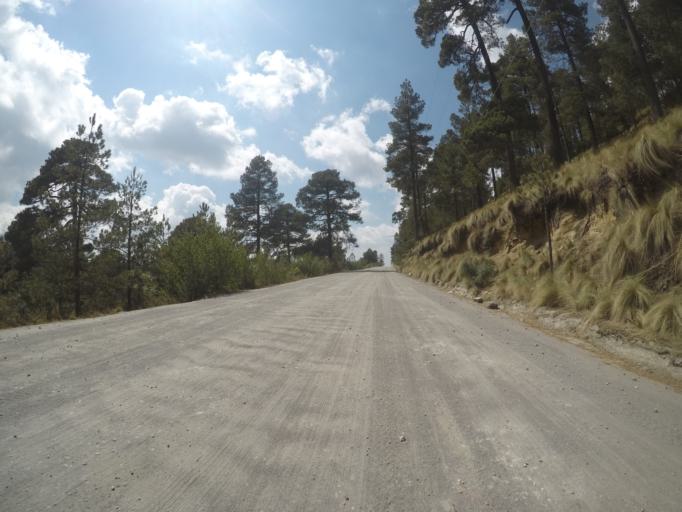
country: MX
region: Mexico
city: Cerro La Calera
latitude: 19.1334
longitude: -99.7932
